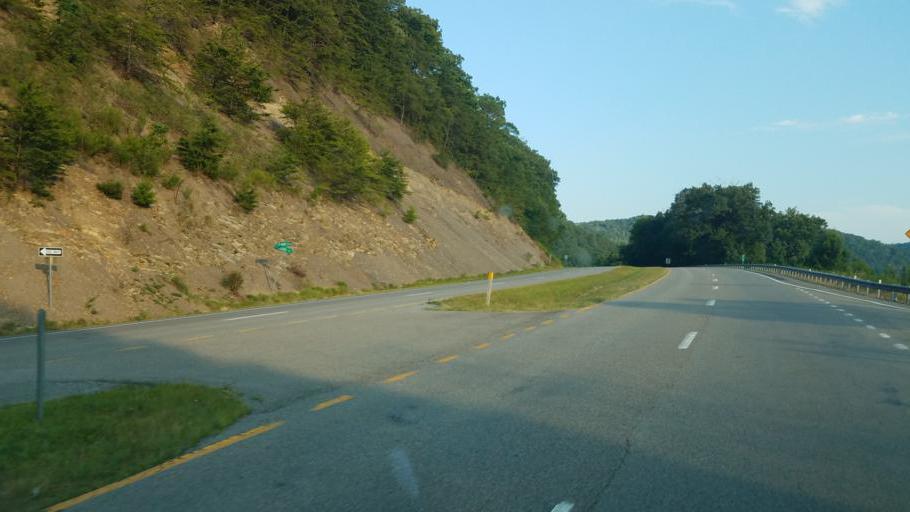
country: US
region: Virginia
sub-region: Lee County
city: Dryden
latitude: 36.7223
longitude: -82.7986
